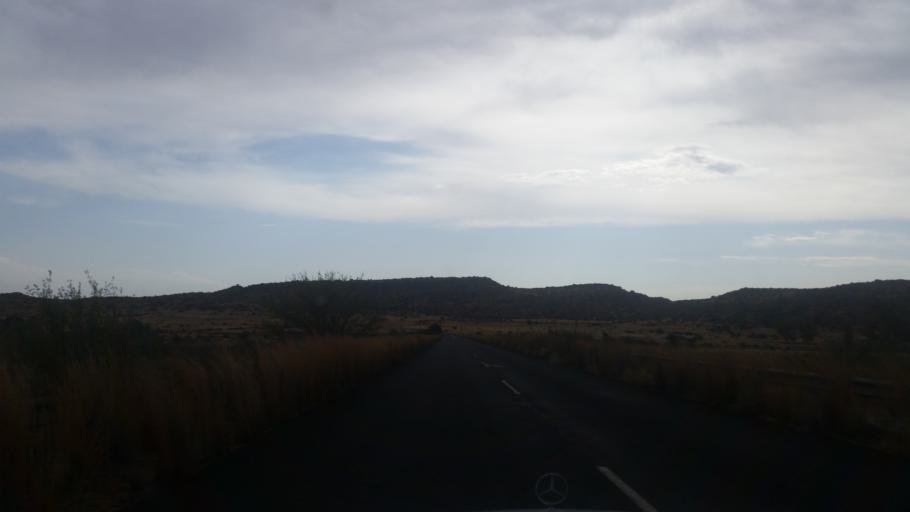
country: ZA
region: Orange Free State
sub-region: Xhariep District Municipality
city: Trompsburg
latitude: -30.4259
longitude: 26.1141
